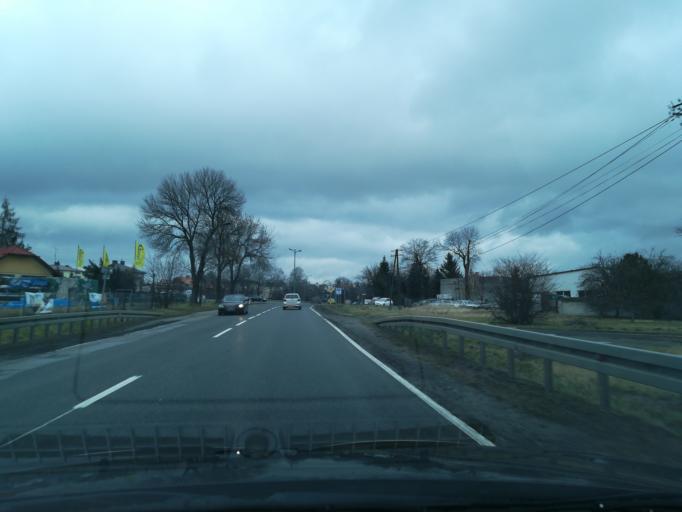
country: PL
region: Subcarpathian Voivodeship
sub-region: Powiat lancucki
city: Lancut
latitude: 50.0722
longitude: 22.2487
